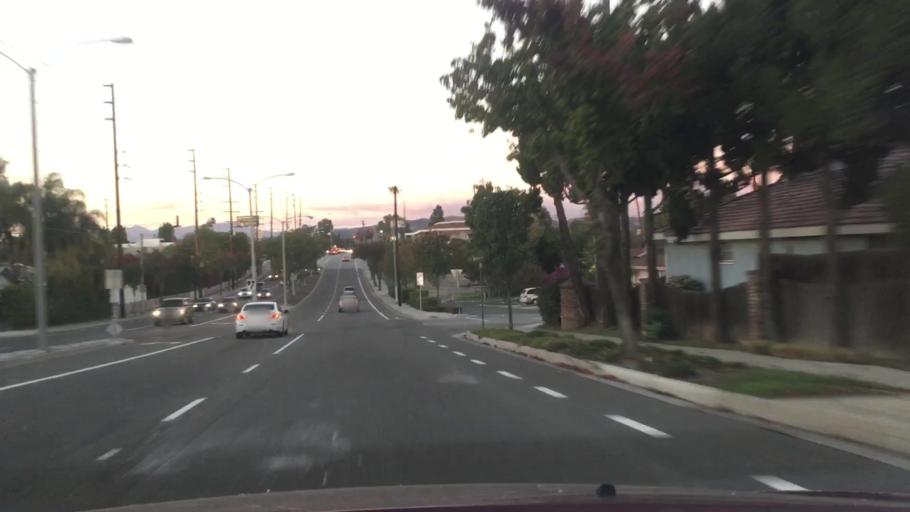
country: US
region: California
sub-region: Los Angeles County
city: La Mirada
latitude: 33.9236
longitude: -118.0118
